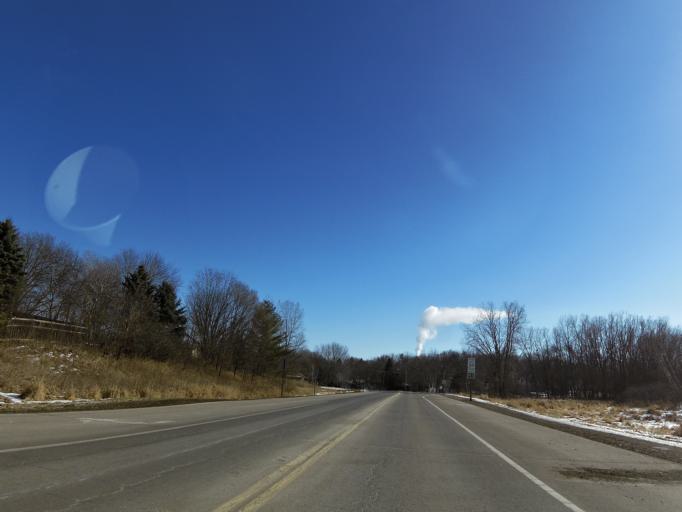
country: US
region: Minnesota
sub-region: Washington County
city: Stillwater
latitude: 45.0559
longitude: -92.8290
